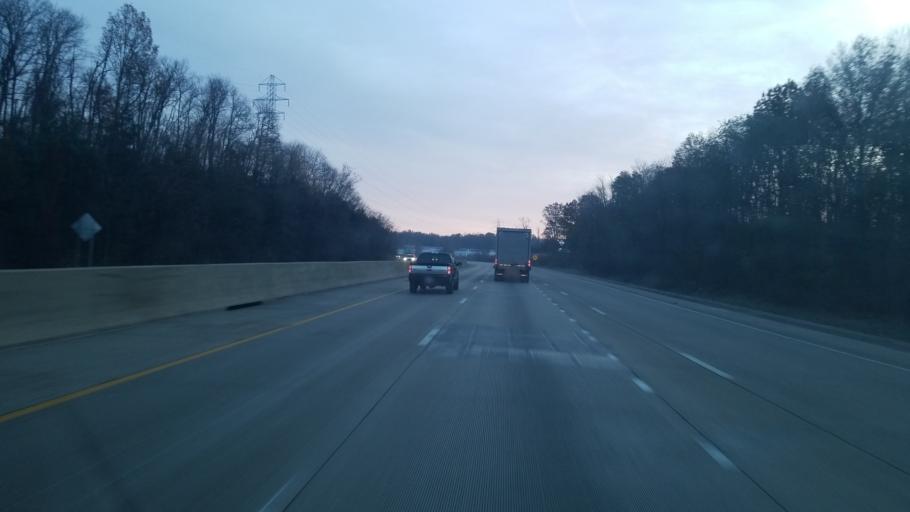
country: US
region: Ohio
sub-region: Summit County
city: Sawyerwood
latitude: 41.0662
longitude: -81.4307
